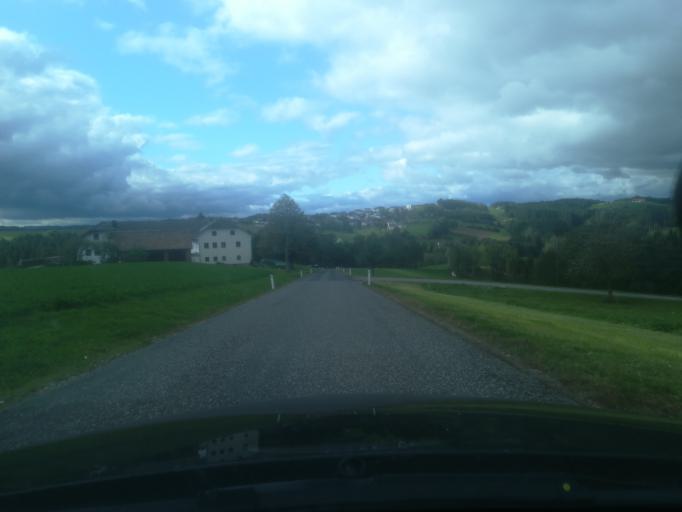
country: AT
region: Upper Austria
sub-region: Politischer Bezirk Urfahr-Umgebung
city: Herzogsdorf
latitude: 48.4245
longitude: 14.1434
